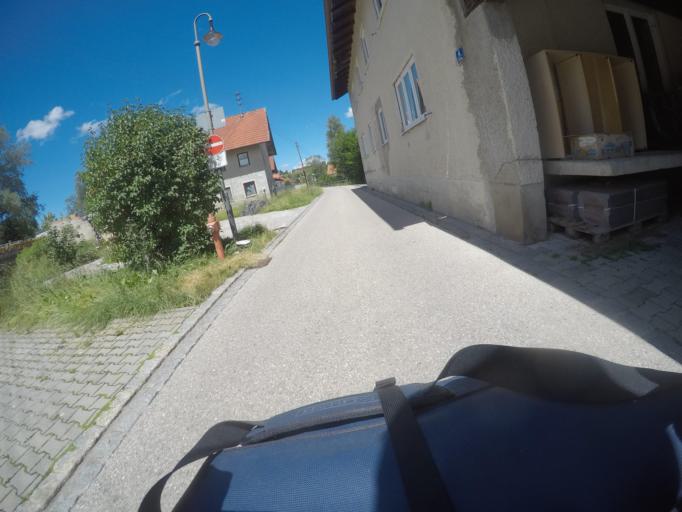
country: DE
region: Bavaria
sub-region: Swabia
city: Lechbruck
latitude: 47.6971
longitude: 10.7954
